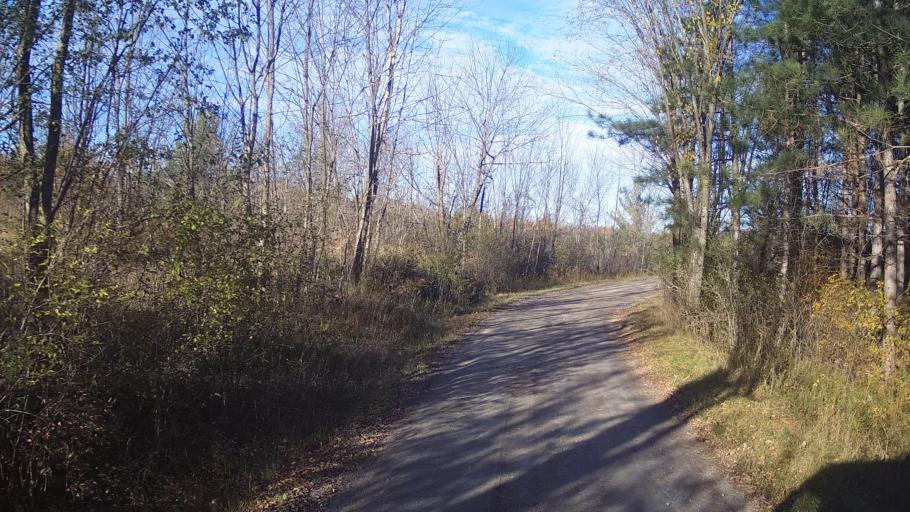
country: CA
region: Ontario
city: Perth
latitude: 44.7379
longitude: -76.4161
